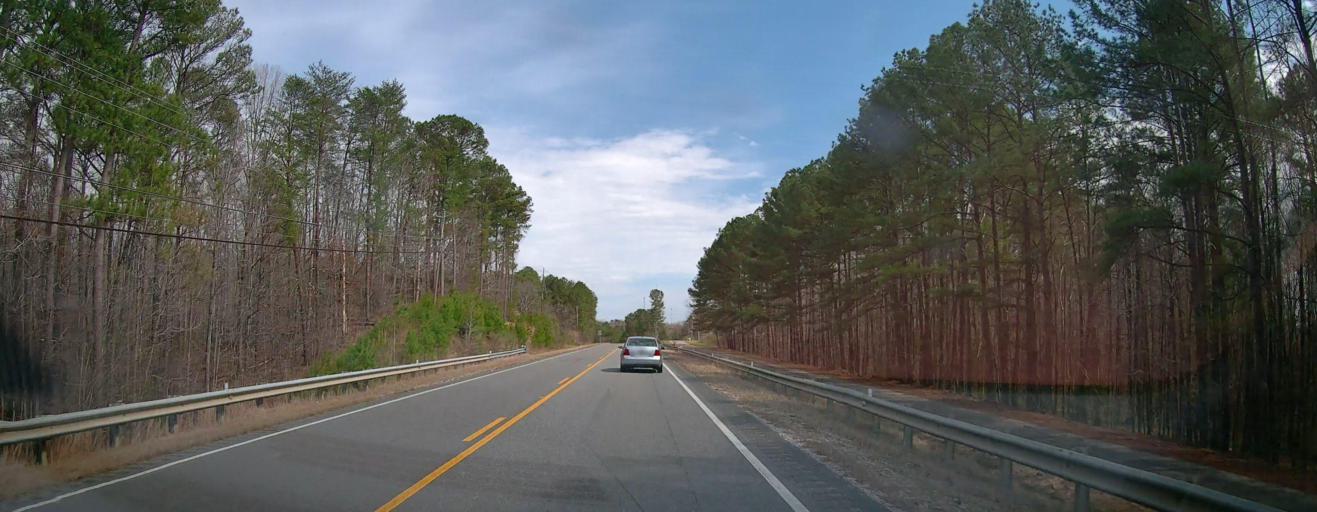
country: US
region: Alabama
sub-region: Walker County
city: Carbon Hill
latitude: 33.9202
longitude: -87.5822
